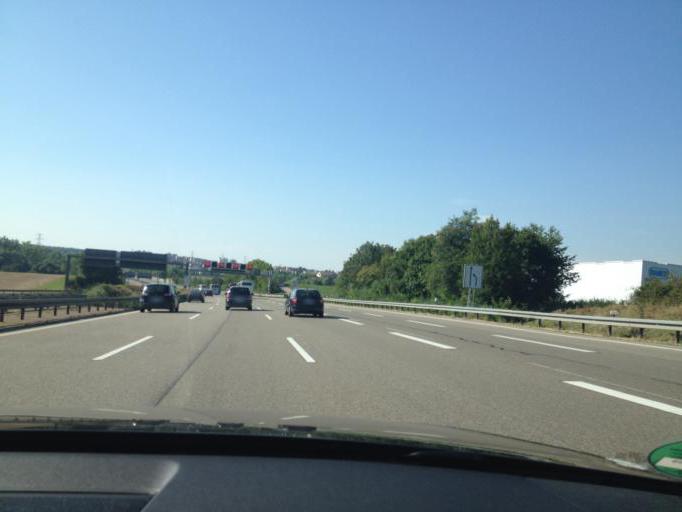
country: DE
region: Baden-Wuerttemberg
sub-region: Regierungsbezirk Stuttgart
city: Asperg
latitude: 48.9174
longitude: 9.1551
